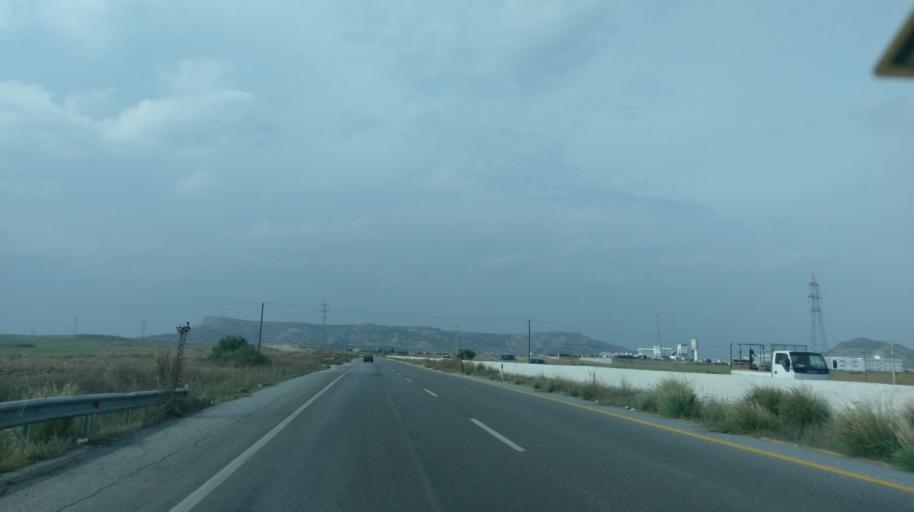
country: CY
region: Lefkosia
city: Mammari
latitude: 35.2208
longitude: 33.1642
